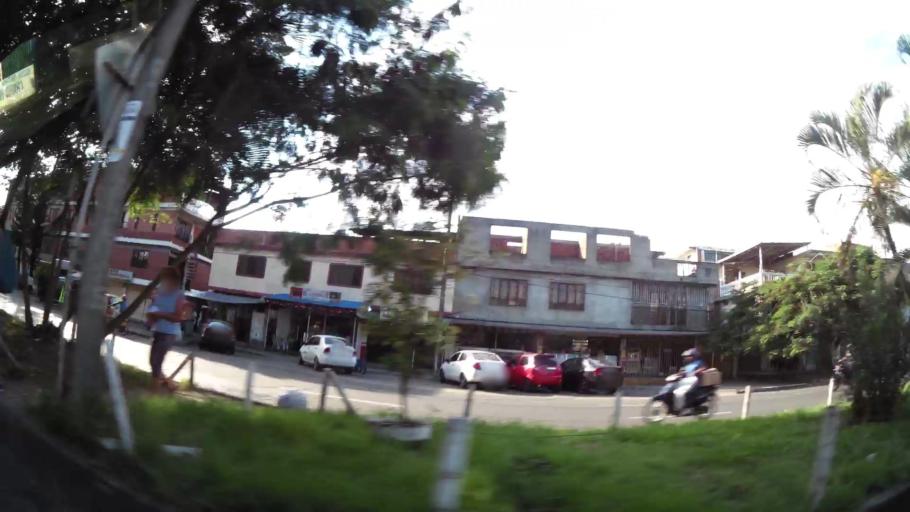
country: CO
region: Valle del Cauca
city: Cali
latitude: 3.4035
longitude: -76.5026
